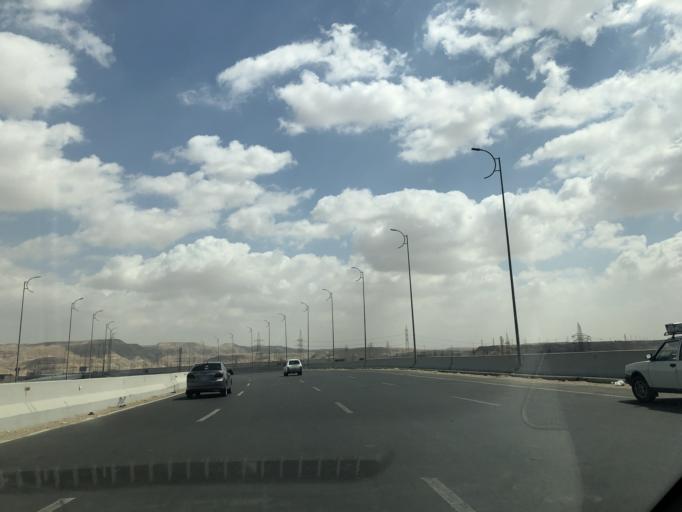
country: EG
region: Muhafazat al Qahirah
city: Halwan
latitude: 29.8741
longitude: 31.3156
